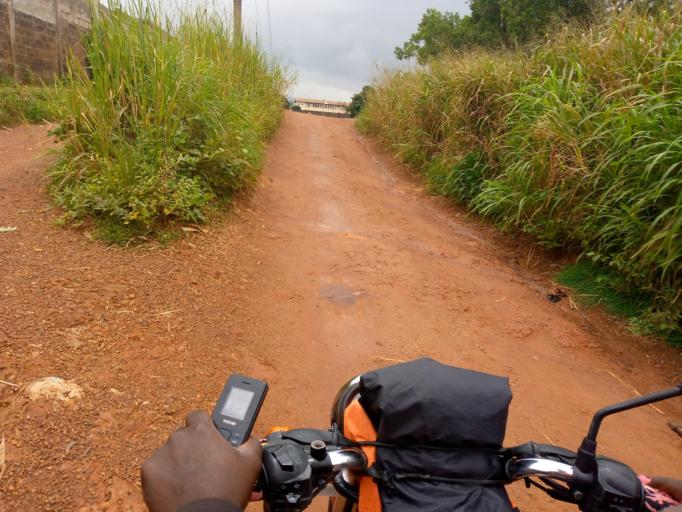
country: SL
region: Eastern Province
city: Kenema
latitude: 7.8734
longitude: -11.1834
